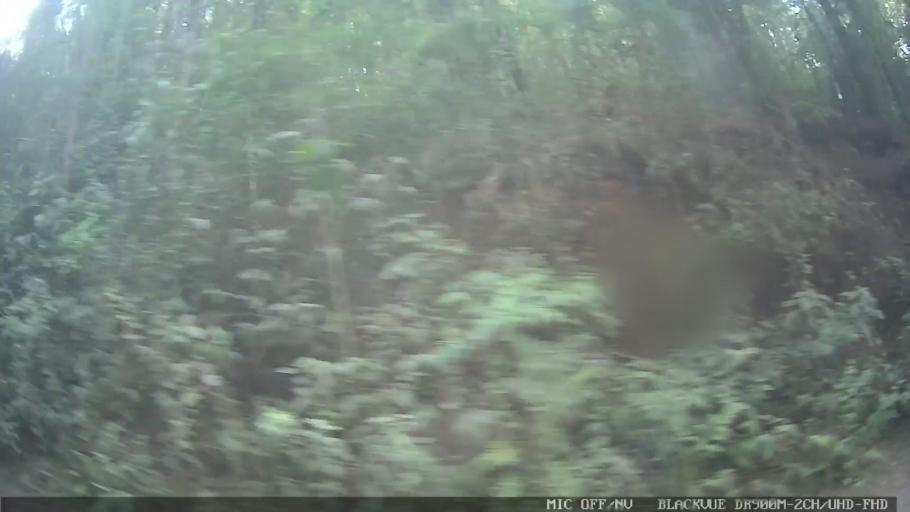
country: BR
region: Sao Paulo
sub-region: Atibaia
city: Atibaia
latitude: -23.1708
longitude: -46.5201
